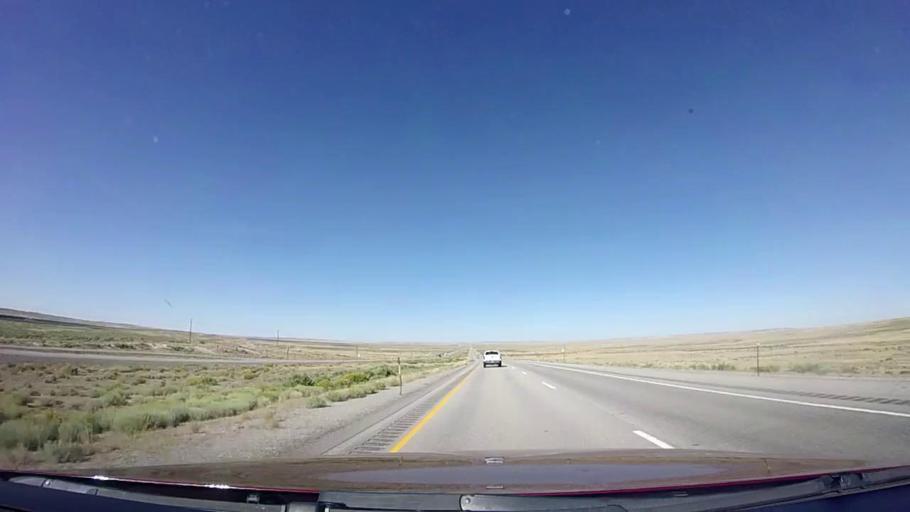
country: US
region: Wyoming
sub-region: Carbon County
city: Rawlins
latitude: 41.7852
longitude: -107.4125
